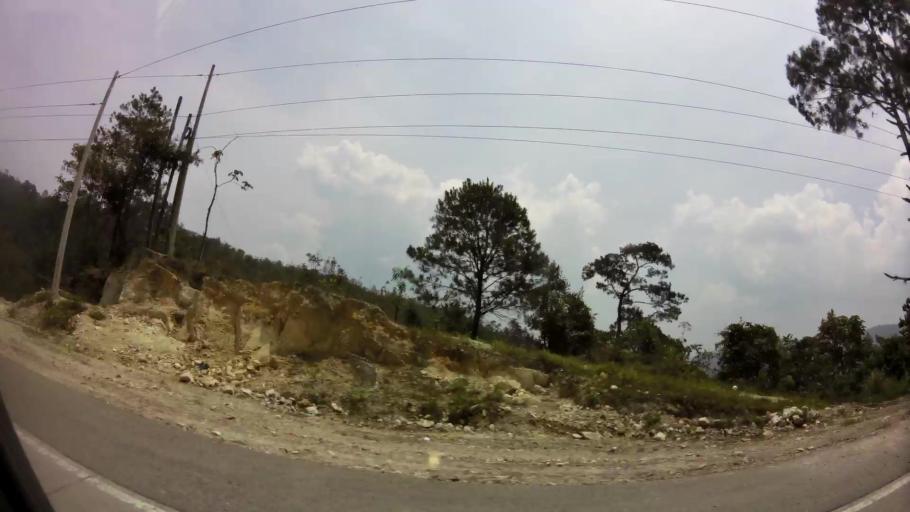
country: HN
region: Comayagua
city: El Socorro
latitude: 14.6542
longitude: -87.9374
